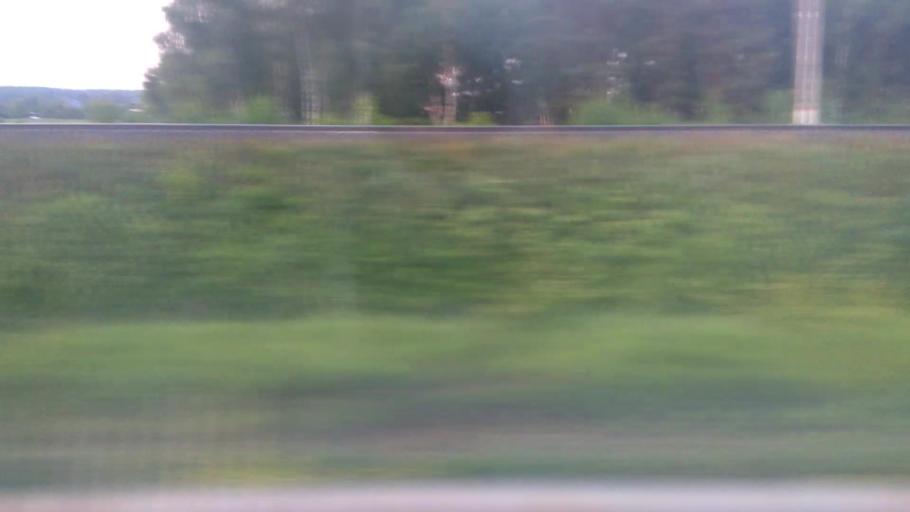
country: RU
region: Moskovskaya
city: Vostryakovo
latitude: 55.3715
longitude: 37.8228
